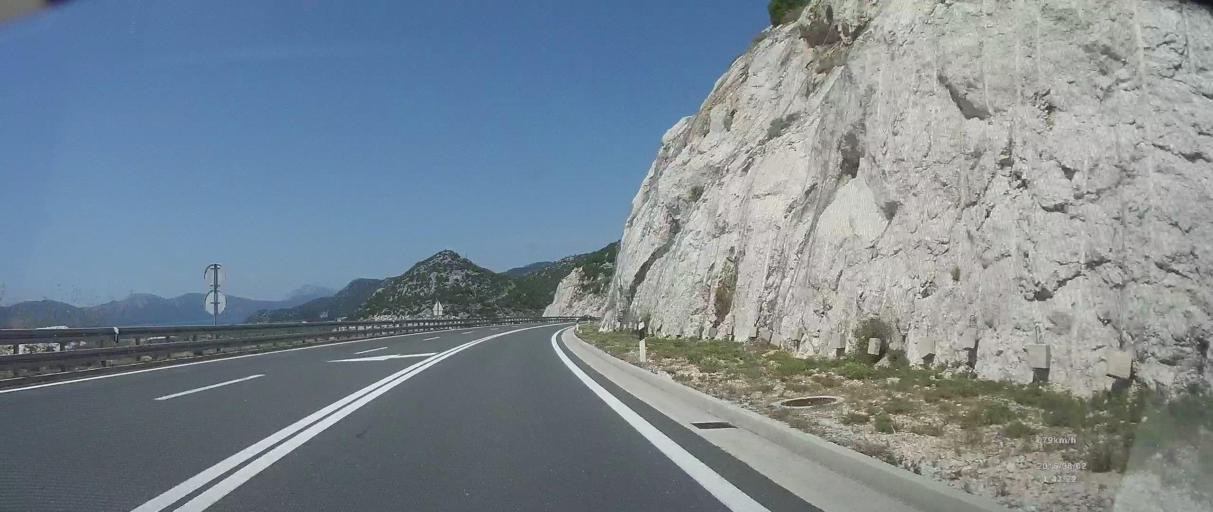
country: HR
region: Dubrovacko-Neretvanska
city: Komin
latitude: 43.0543
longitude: 17.4723
